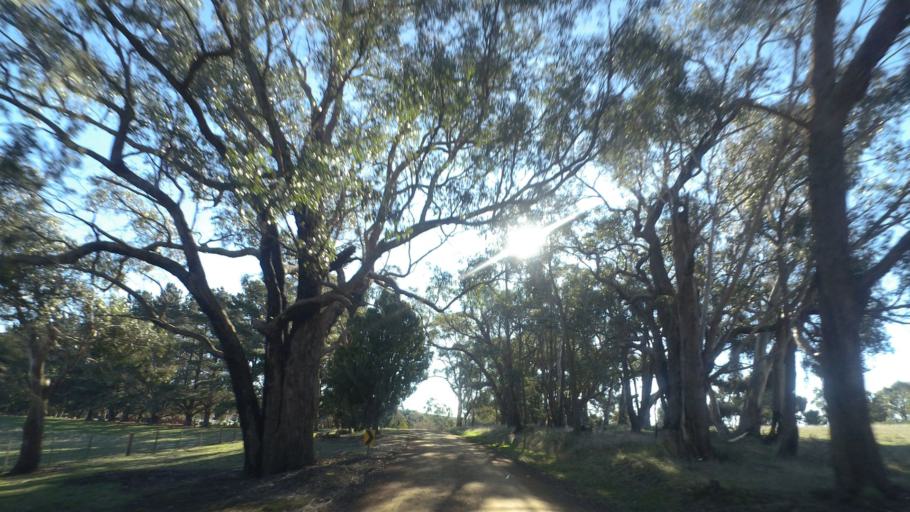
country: AU
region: Victoria
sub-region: Mount Alexander
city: Castlemaine
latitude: -37.2946
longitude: 144.3314
